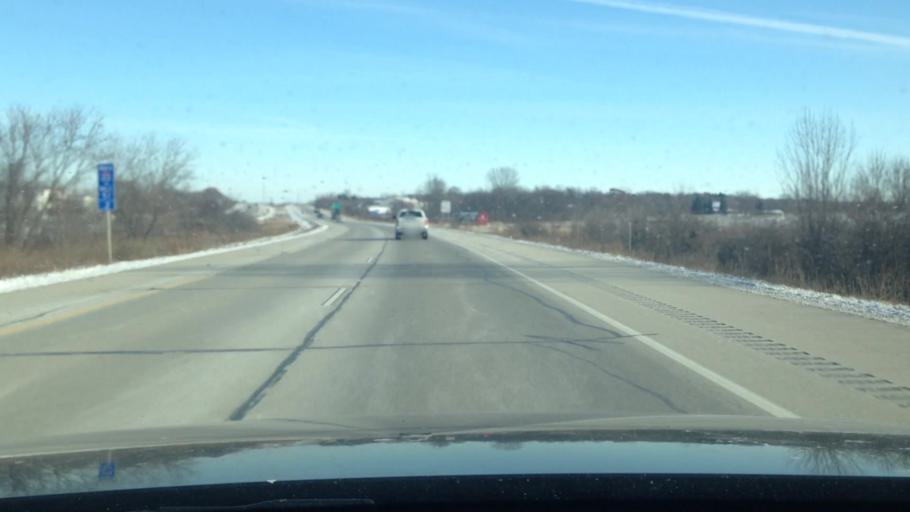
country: US
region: Wisconsin
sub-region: Waukesha County
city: Big Bend
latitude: 42.9138
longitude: -88.2082
